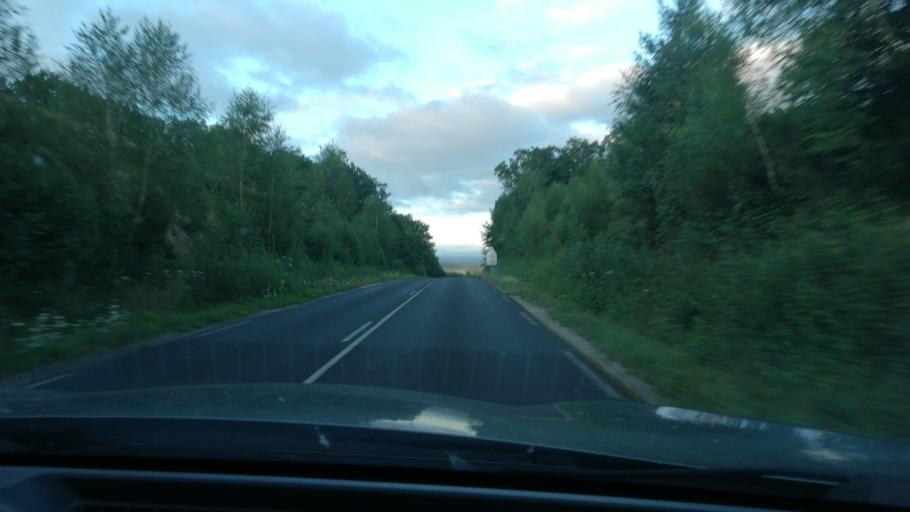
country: FR
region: Auvergne
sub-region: Departement du Cantal
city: Laroquebrou
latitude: 44.9589
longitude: 2.1560
